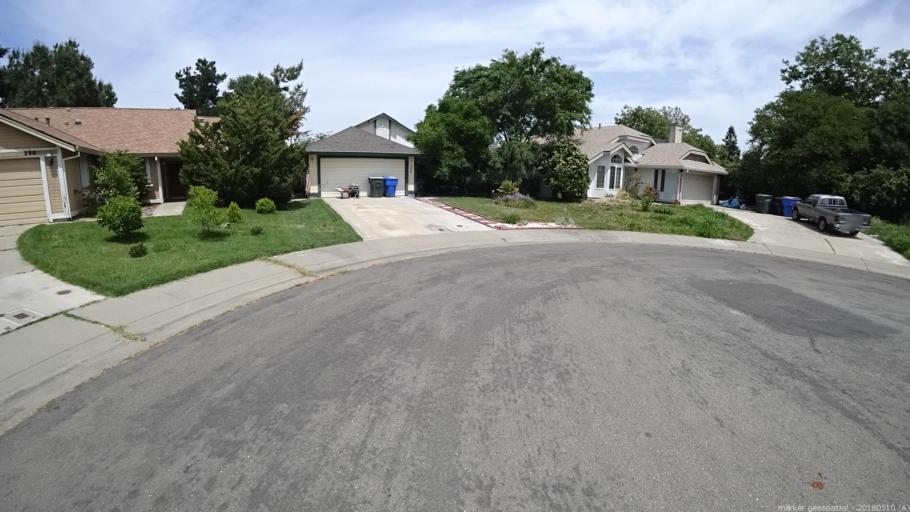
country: US
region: California
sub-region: Sacramento County
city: Rio Linda
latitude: 38.6592
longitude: -121.4635
